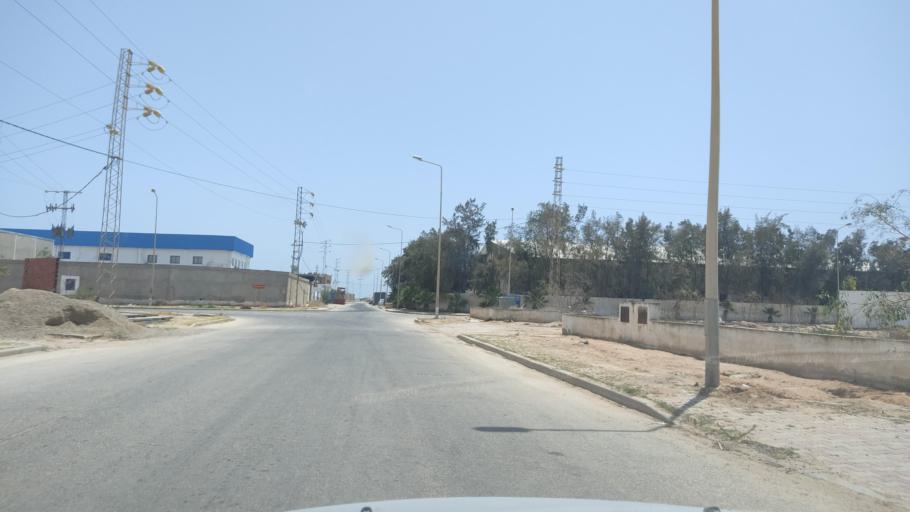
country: TN
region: Safaqis
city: Sfax
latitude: 34.6621
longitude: 10.6977
